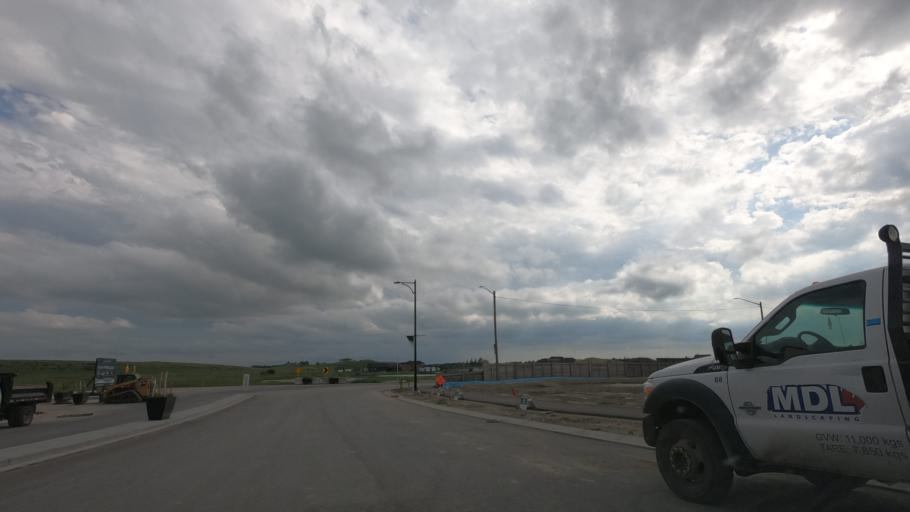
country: CA
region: Alberta
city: Airdrie
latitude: 51.2569
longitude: -113.9815
